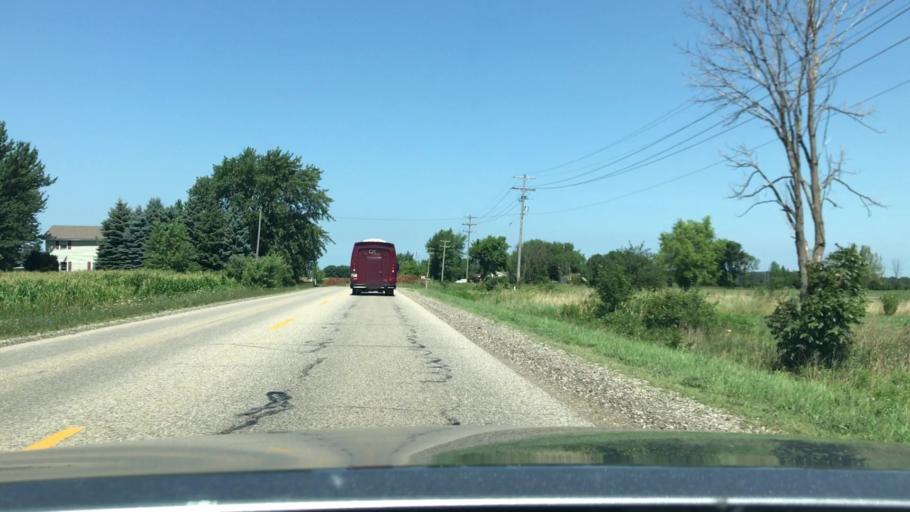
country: US
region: Michigan
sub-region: Ottawa County
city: Zeeland
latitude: 42.8648
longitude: -86.0797
